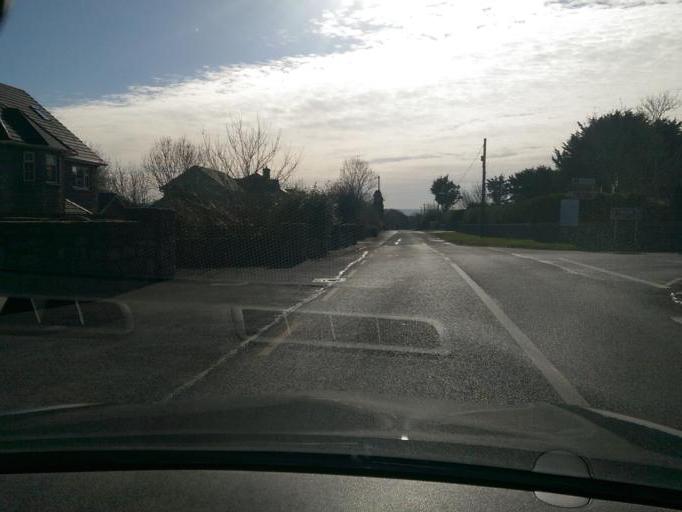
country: IE
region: Connaught
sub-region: County Galway
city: Oranmore
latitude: 53.2455
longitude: -8.9547
